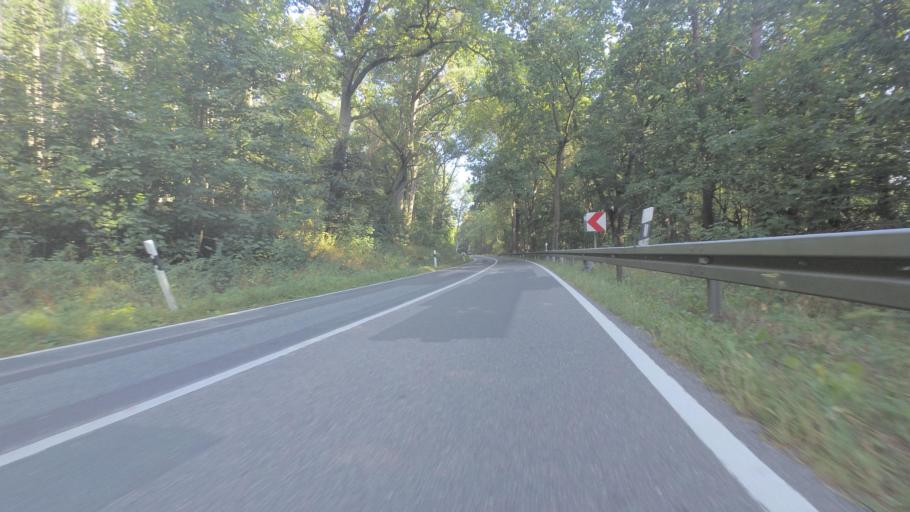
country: DE
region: Mecklenburg-Vorpommern
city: Malchow
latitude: 53.4529
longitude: 12.4313
